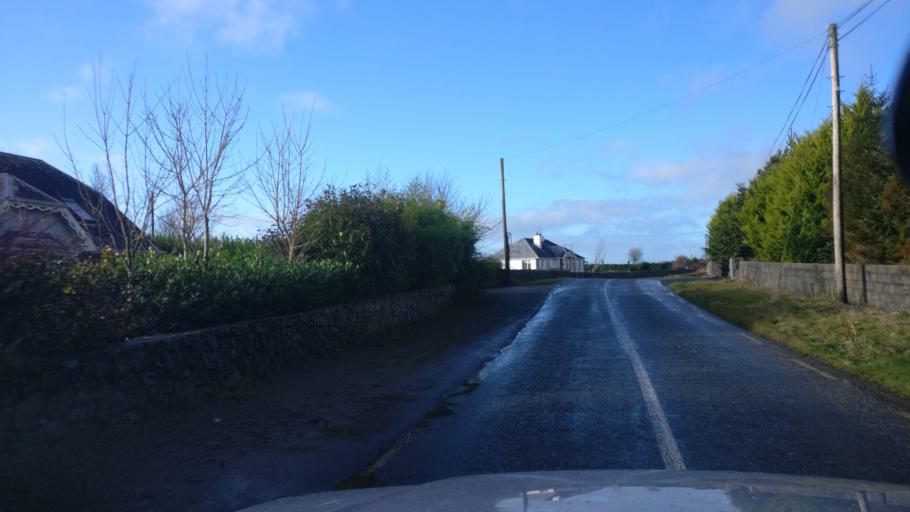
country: IE
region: Connaught
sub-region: County Galway
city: Athenry
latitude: 53.2638
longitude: -8.6860
